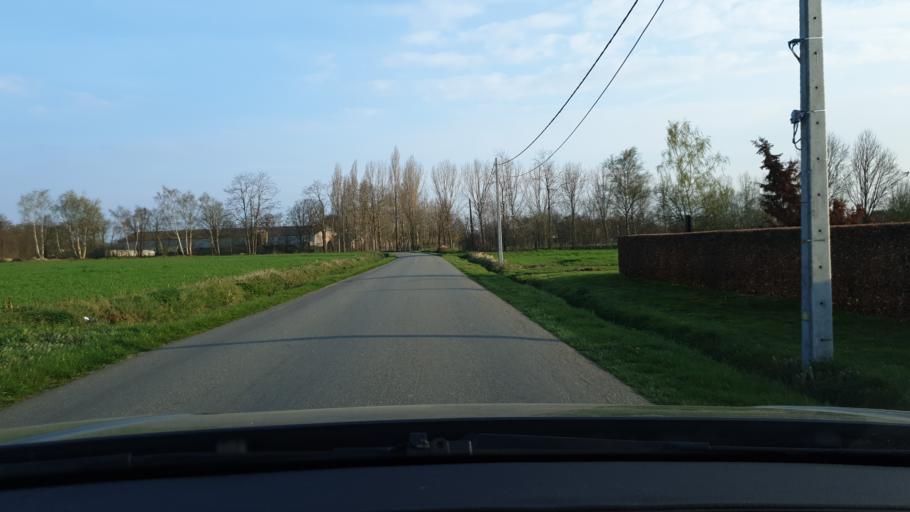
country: BE
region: Flanders
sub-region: Provincie Antwerpen
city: Geel
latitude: 51.1473
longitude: 4.9655
